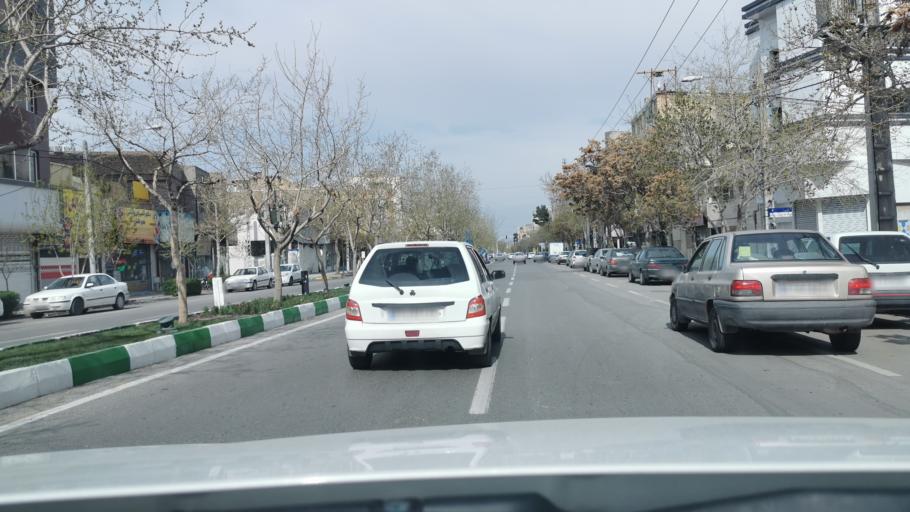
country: IR
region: Razavi Khorasan
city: Mashhad
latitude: 36.3193
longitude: 59.6024
